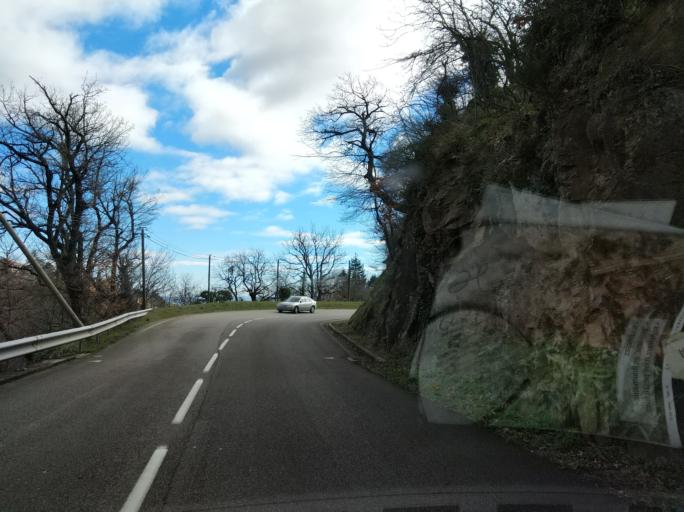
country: FR
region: Rhone-Alpes
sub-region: Departement de la Loire
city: Pelussin
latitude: 45.4152
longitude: 4.6678
